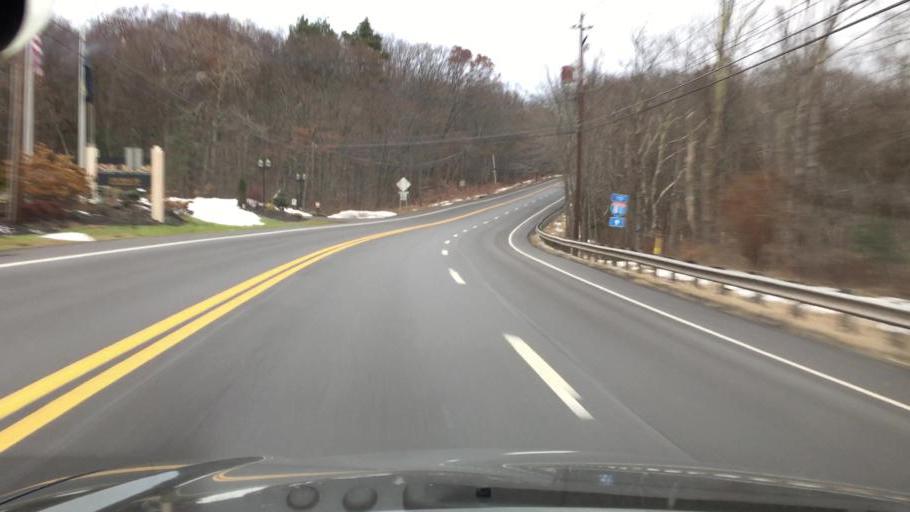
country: US
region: Pennsylvania
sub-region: Luzerne County
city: Freeland
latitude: 41.0635
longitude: -75.9644
